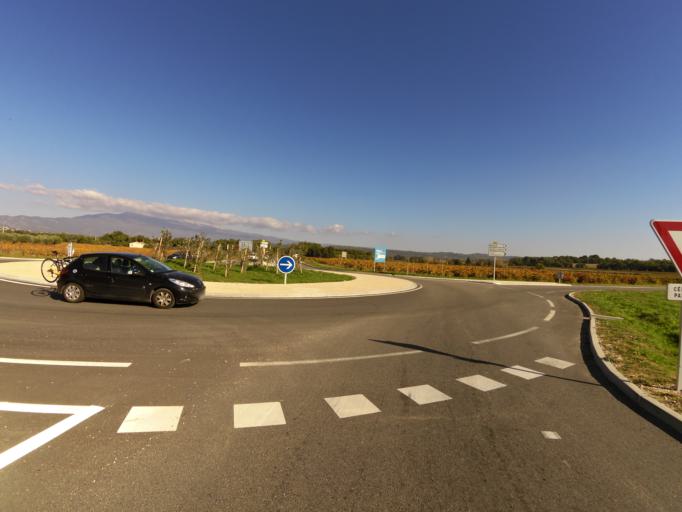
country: FR
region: Provence-Alpes-Cote d'Azur
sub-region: Departement du Vaucluse
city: Caromb
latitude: 44.0843
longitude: 5.1157
